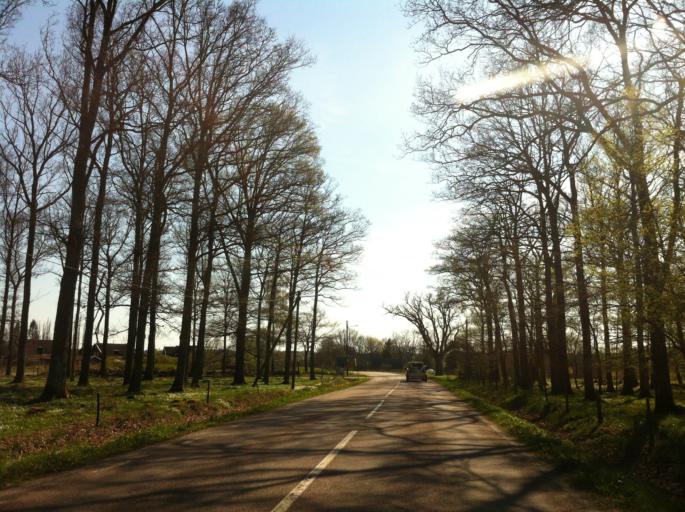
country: SE
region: Skane
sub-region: Svalovs Kommun
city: Kagerod
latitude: 56.0408
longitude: 13.1022
